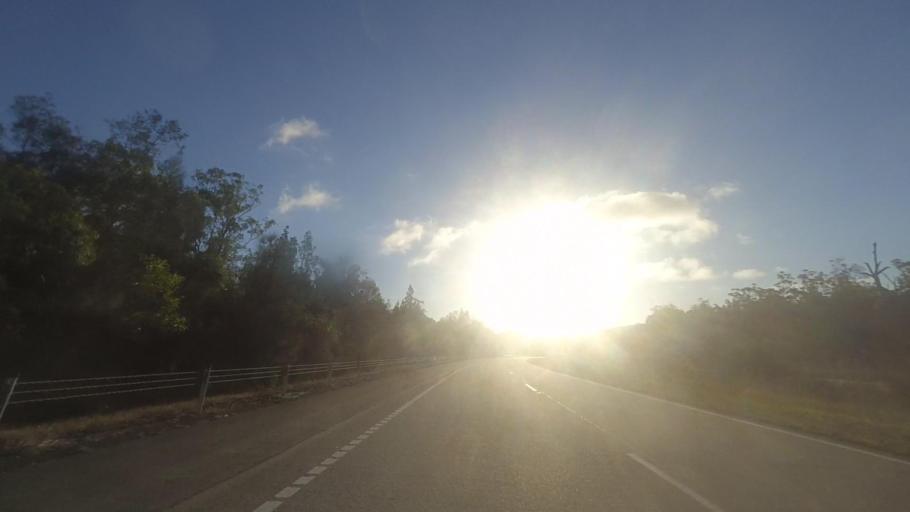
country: AU
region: New South Wales
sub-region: Great Lakes
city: Hawks Nest
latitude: -32.5470
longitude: 152.1599
